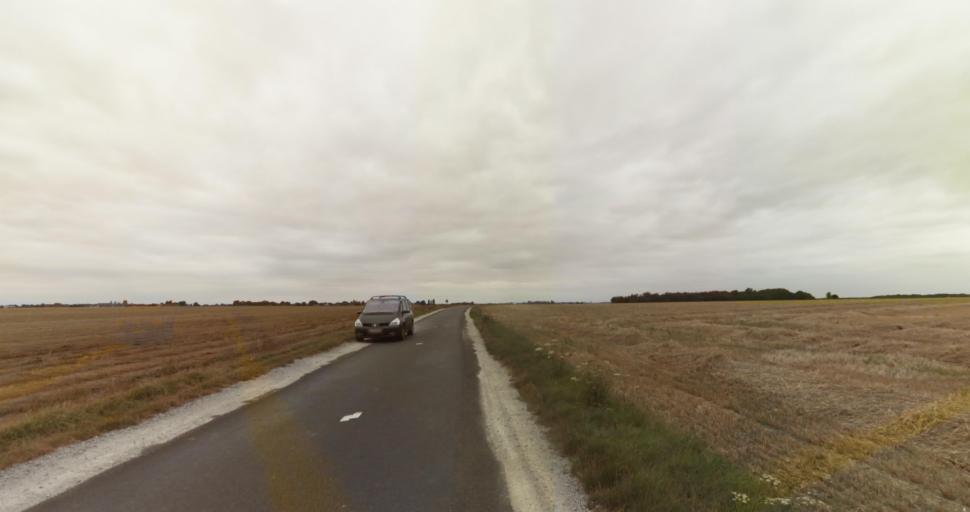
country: FR
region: Haute-Normandie
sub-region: Departement de l'Eure
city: Evreux
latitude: 48.9602
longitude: 1.2393
